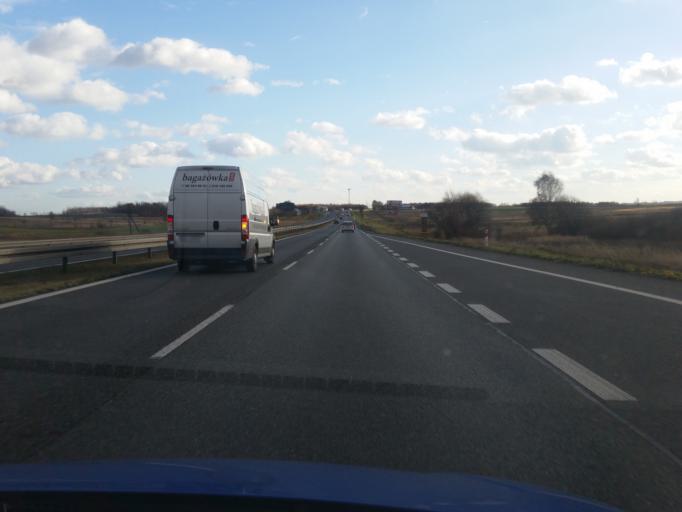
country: PL
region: Silesian Voivodeship
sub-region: Powiat myszkowski
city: Kozieglowy
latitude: 50.6211
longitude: 19.1463
